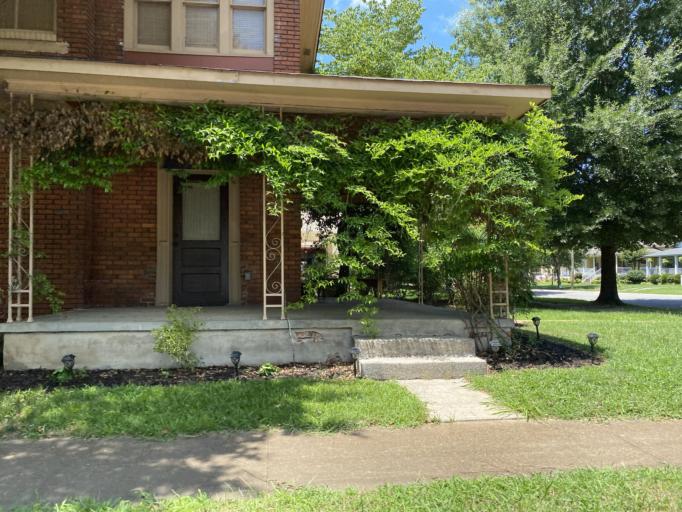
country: US
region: Alabama
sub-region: Morgan County
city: Decatur
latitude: 34.5995
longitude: -86.9802
